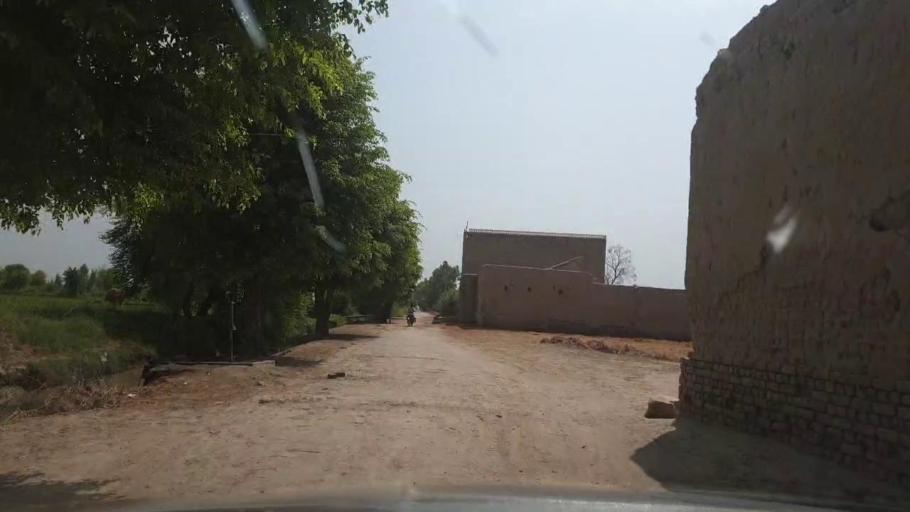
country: PK
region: Sindh
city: Ratodero
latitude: 27.8794
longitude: 68.3313
